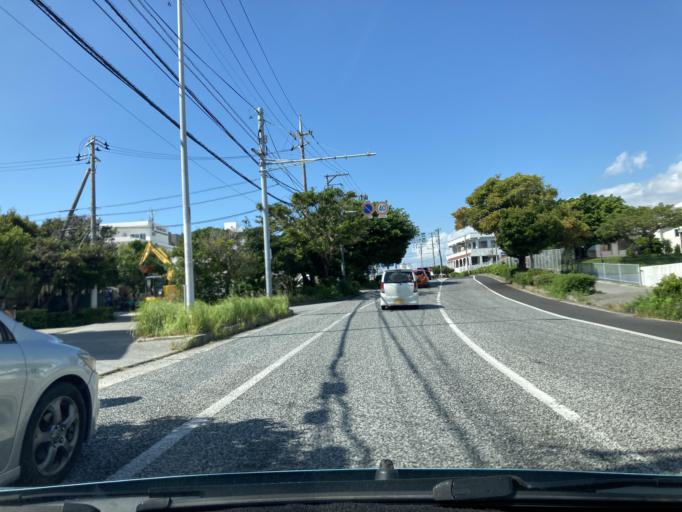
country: JP
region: Okinawa
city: Ginowan
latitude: 26.2549
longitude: 127.7549
